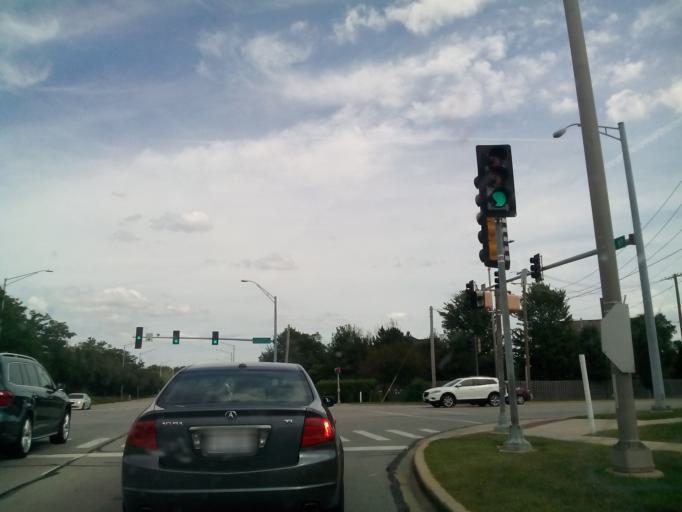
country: US
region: Illinois
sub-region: DuPage County
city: Naperville
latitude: 41.7104
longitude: -88.1675
